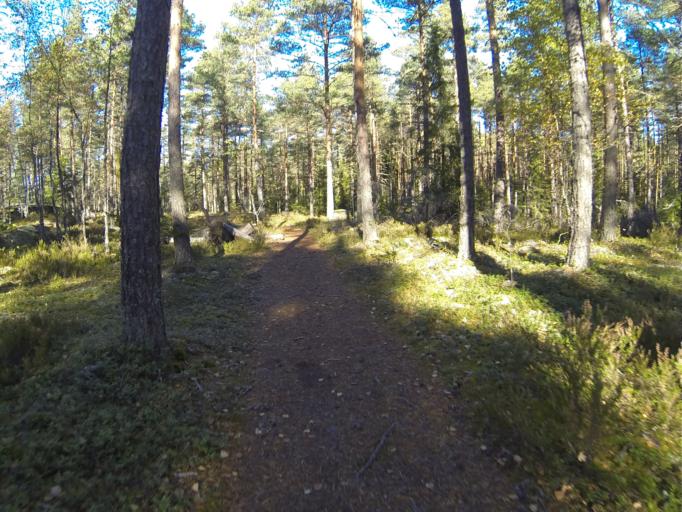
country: FI
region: Varsinais-Suomi
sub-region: Salo
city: Saerkisalo
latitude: 60.2047
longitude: 22.9221
